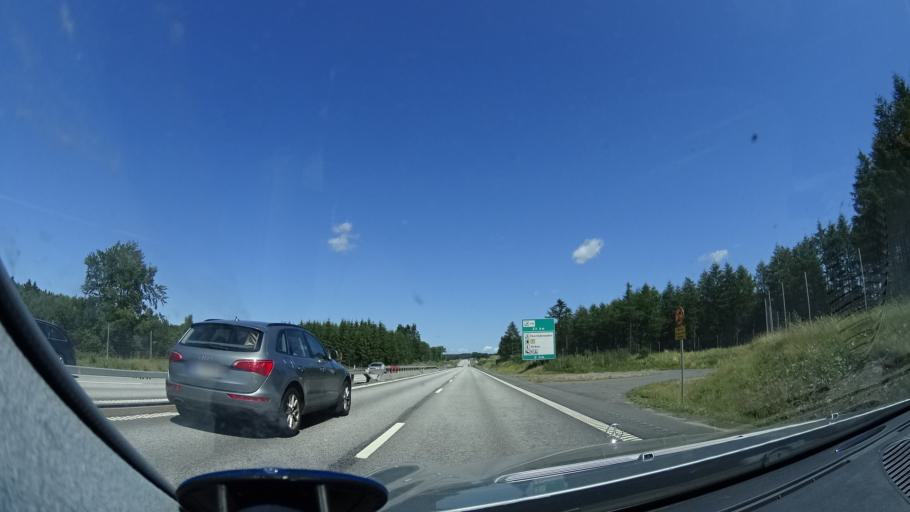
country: SE
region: Skane
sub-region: Horby Kommun
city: Hoerby
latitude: 55.8794
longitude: 13.7127
